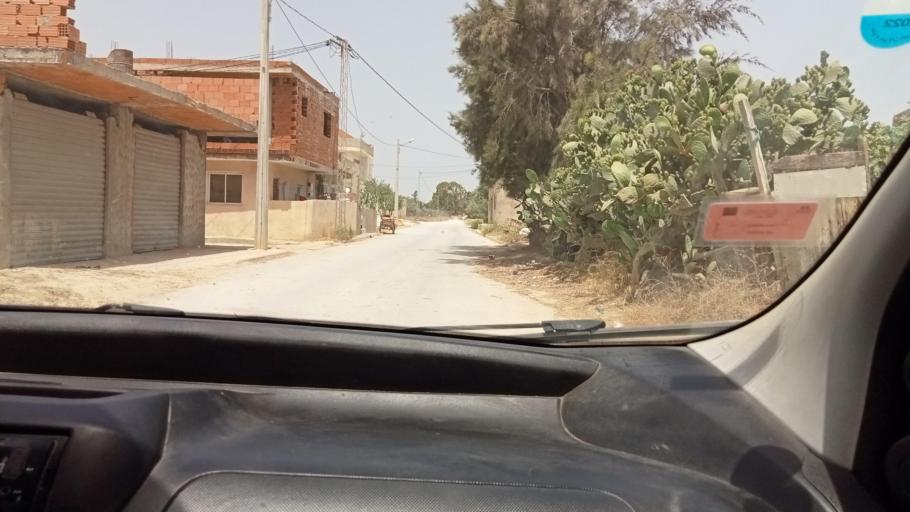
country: TN
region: Nabul
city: Qulaybiyah
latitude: 36.8630
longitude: 11.0849
